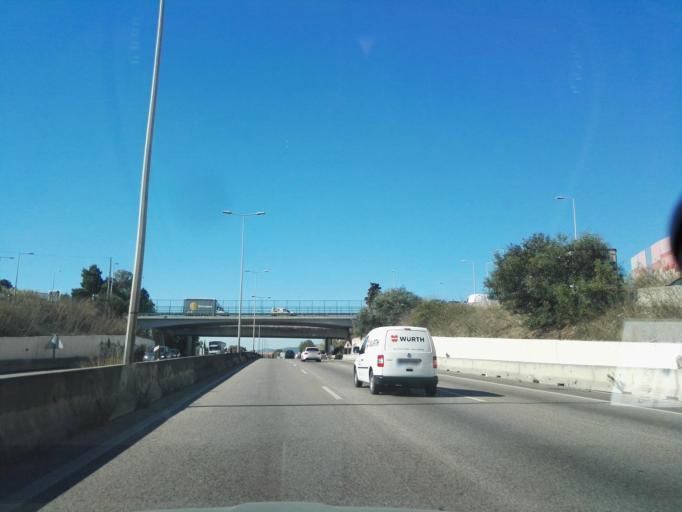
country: PT
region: Lisbon
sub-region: Sintra
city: Cacem
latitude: 38.7660
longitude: -9.3047
